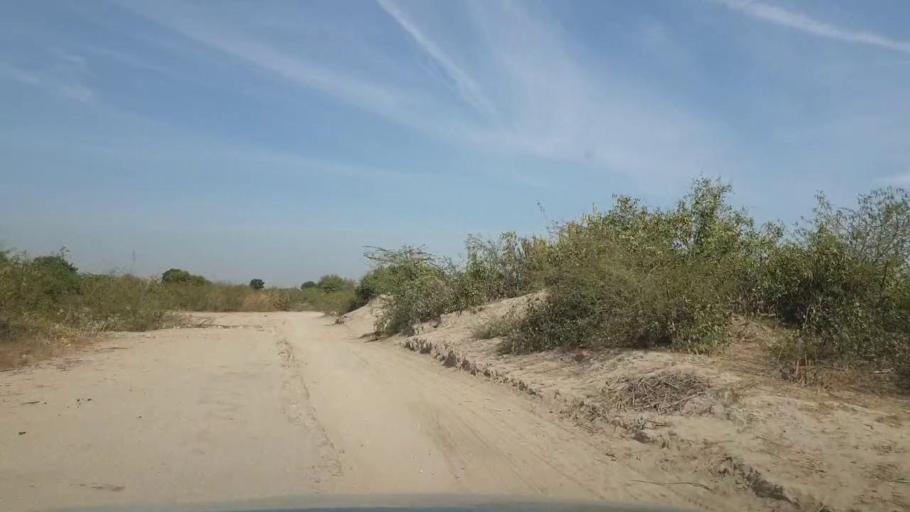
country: PK
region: Sindh
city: Nabisar
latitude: 25.1199
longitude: 69.6378
